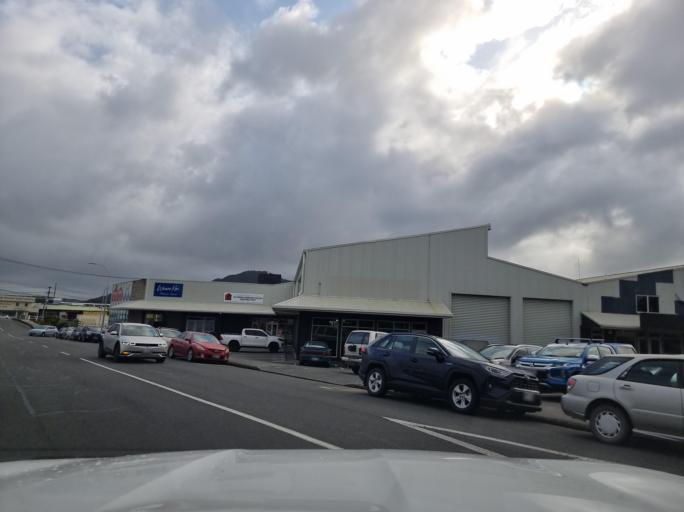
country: NZ
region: Northland
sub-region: Whangarei
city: Whangarei
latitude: -35.7297
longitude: 174.3217
